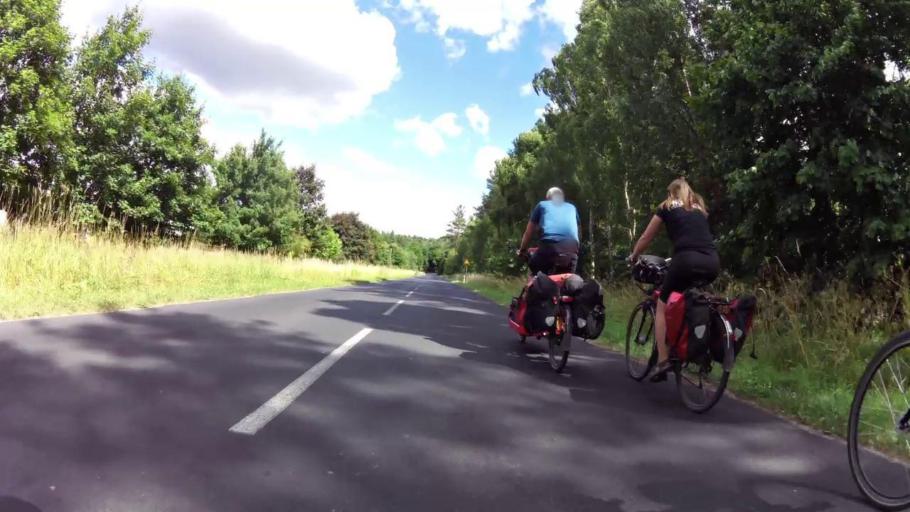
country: PL
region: West Pomeranian Voivodeship
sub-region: Powiat lobeski
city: Lobez
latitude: 53.6536
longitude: 15.5741
